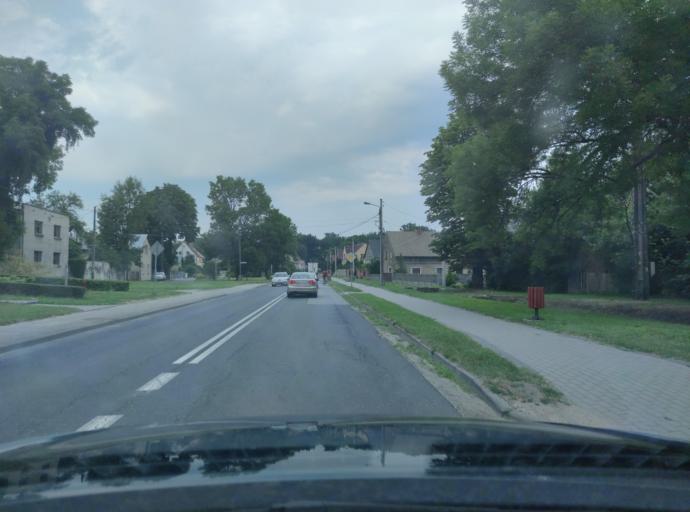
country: PL
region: Opole Voivodeship
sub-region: Powiat strzelecki
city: Strzelce Opolskie
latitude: 50.5051
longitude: 18.2948
